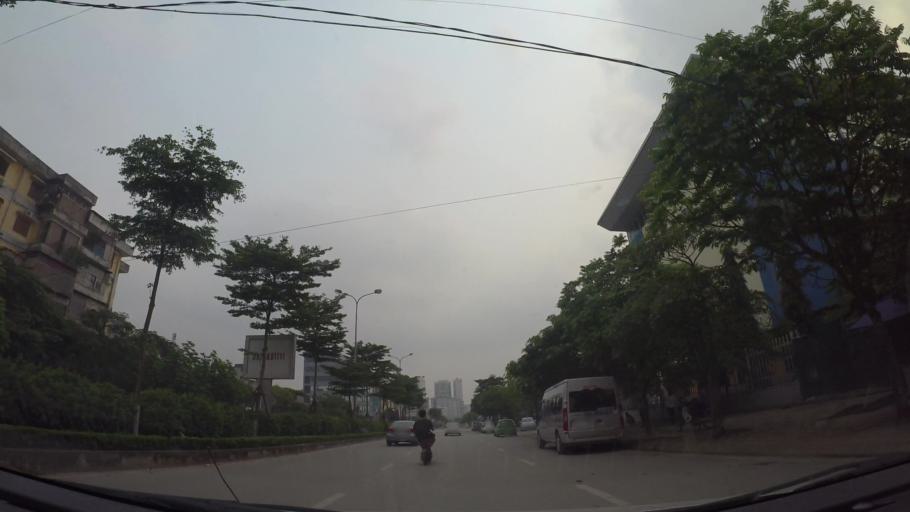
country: VN
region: Ha Noi
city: Cau Dien
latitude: 21.0437
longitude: 105.7740
